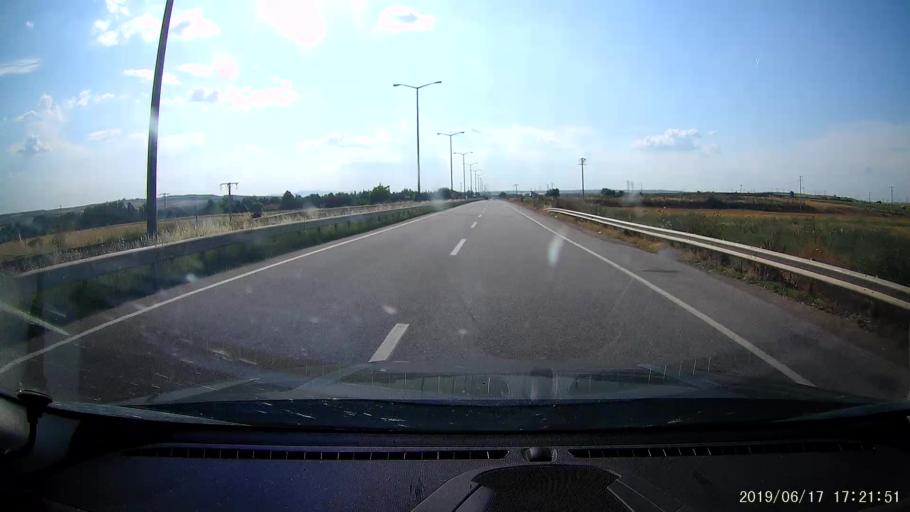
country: GR
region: East Macedonia and Thrace
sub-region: Nomos Evrou
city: Rizia
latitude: 41.7084
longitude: 26.3857
